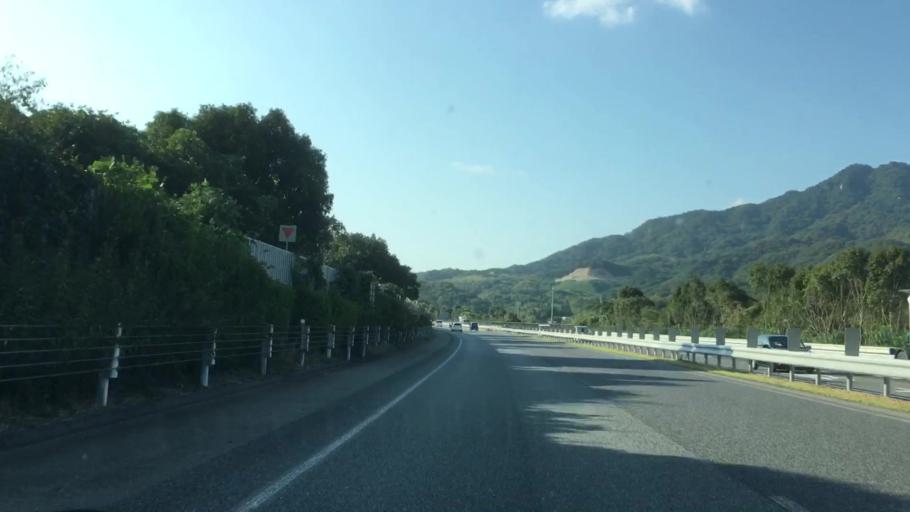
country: JP
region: Yamaguchi
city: Hofu
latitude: 34.0668
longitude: 131.6031
